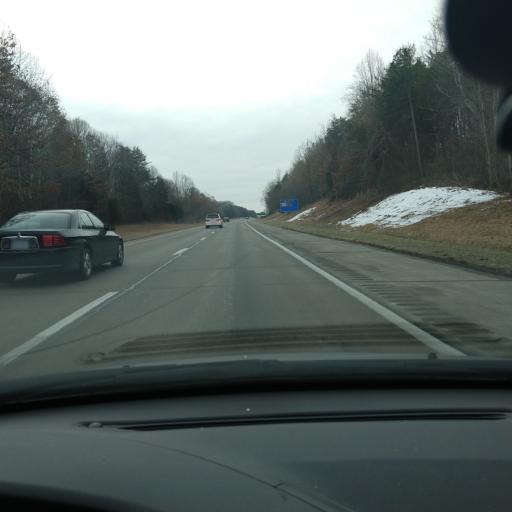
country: US
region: North Carolina
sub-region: Davidson County
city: Midway
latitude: 35.9797
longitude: -80.2332
